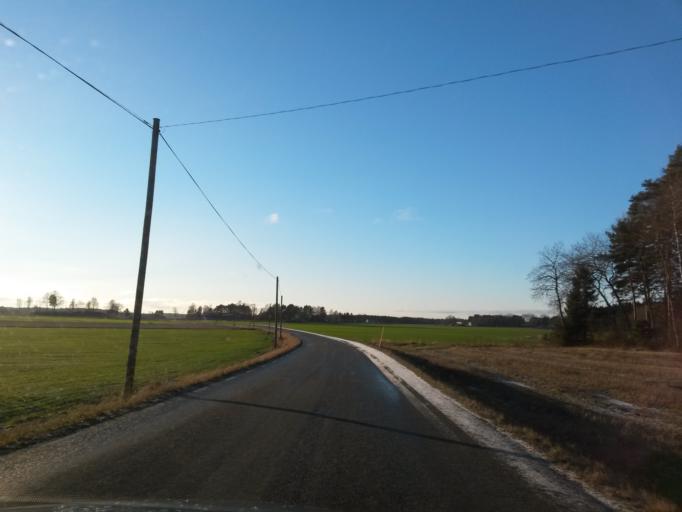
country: SE
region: Vaestra Goetaland
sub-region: Essunga Kommun
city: Nossebro
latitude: 58.2642
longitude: 12.7361
